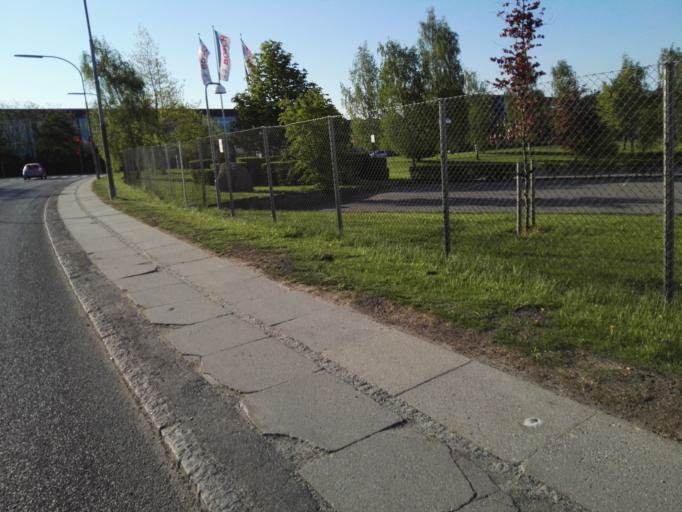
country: DK
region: Capital Region
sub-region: Ballerup Kommune
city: Ballerup
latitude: 55.7326
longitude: 12.3468
